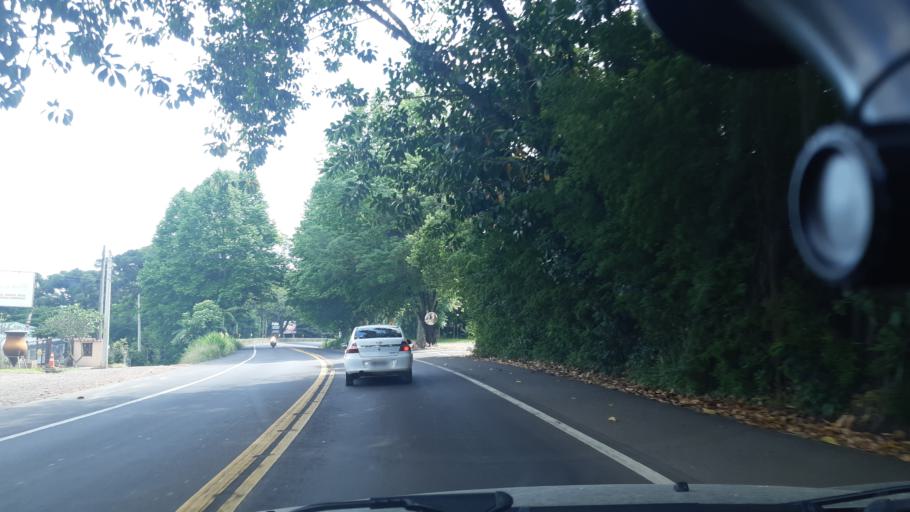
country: BR
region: Rio Grande do Sul
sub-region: Ivoti
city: Ivoti
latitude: -29.6224
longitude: -51.1307
